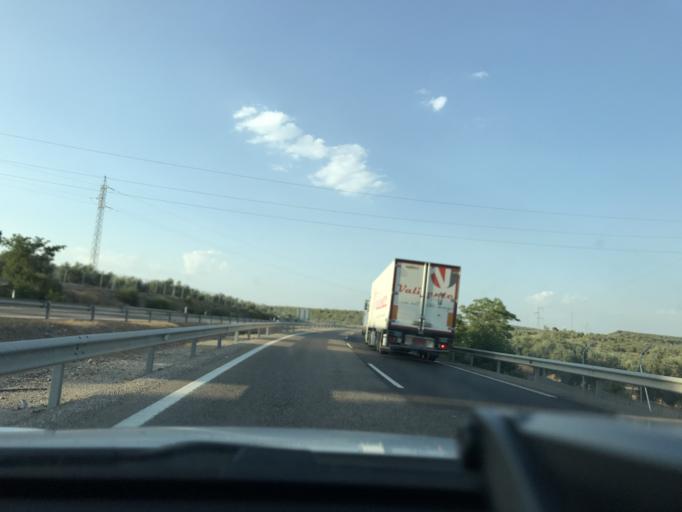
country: ES
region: Andalusia
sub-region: Provincia de Jaen
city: Espeluy
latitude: 38.0577
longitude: -3.8937
